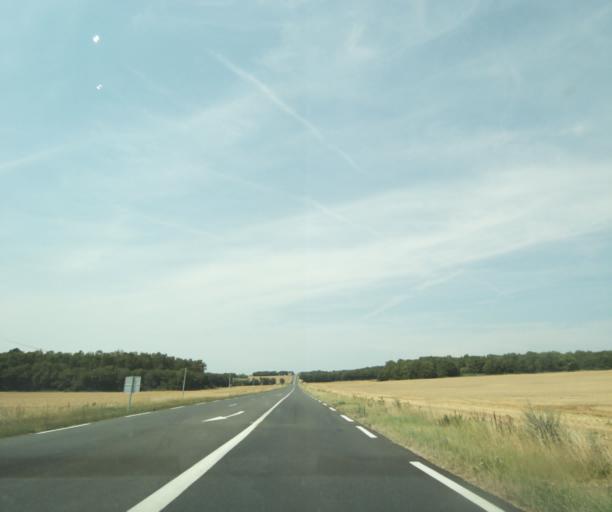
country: FR
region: Centre
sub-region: Departement d'Indre-et-Loire
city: Sainte-Maure-de-Touraine
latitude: 47.0779
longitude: 0.6129
